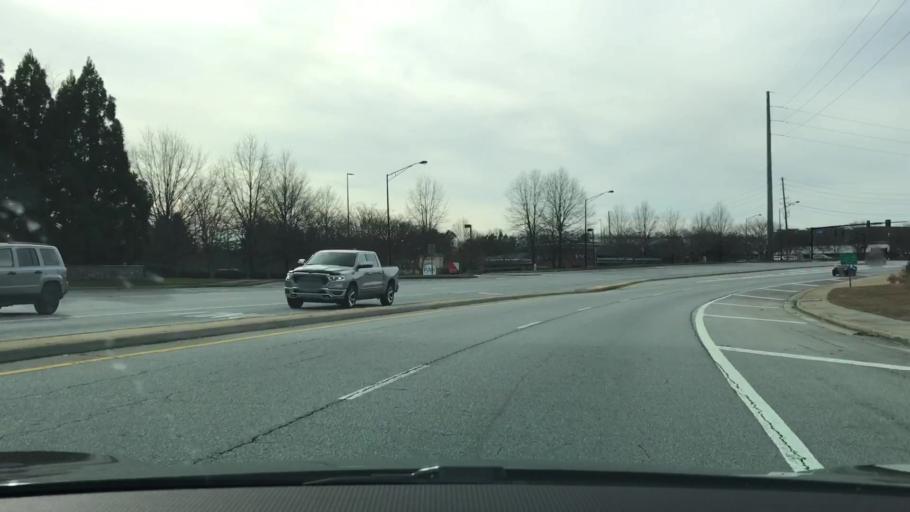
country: US
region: Georgia
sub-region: Gwinnett County
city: Suwanee
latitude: 34.0006
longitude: -84.0673
